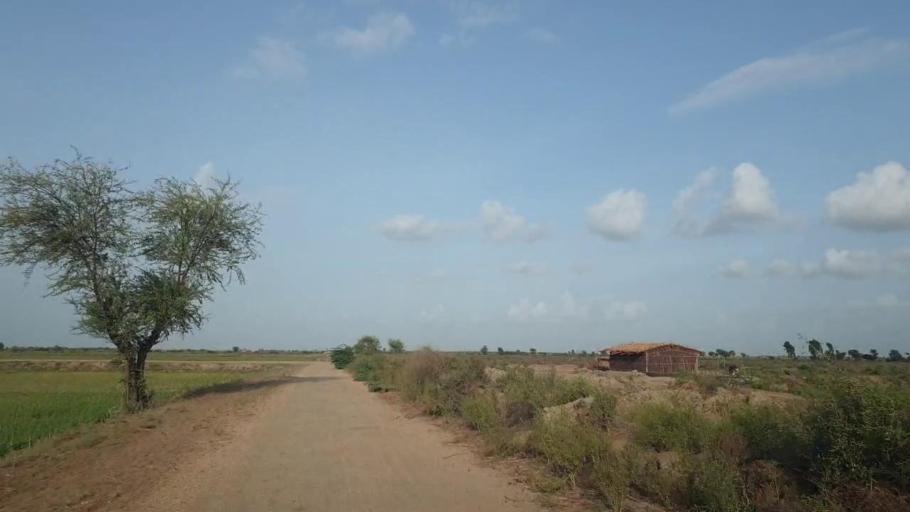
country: PK
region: Sindh
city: Tando Bago
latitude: 24.6627
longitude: 69.1129
